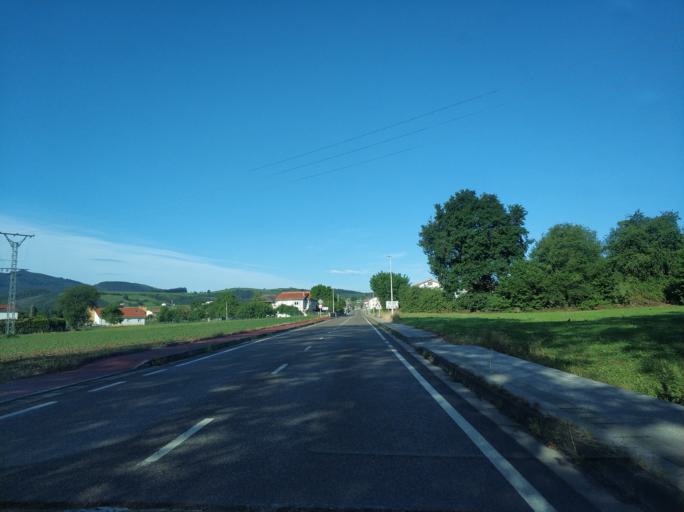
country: ES
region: Cantabria
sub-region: Provincia de Cantabria
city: Polanco
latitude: 43.3511
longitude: -3.9807
